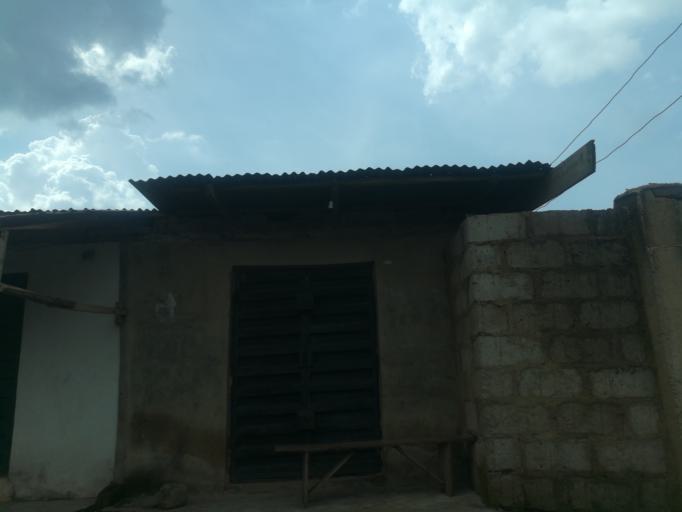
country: NG
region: Oyo
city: Moniya
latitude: 7.4583
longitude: 3.9210
